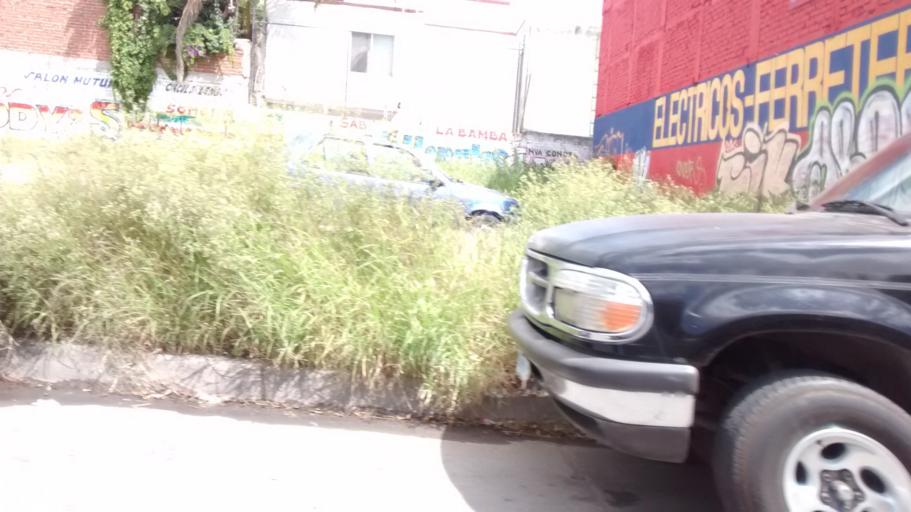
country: MX
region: Guanajuato
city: Leon
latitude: 21.1037
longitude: -101.6487
